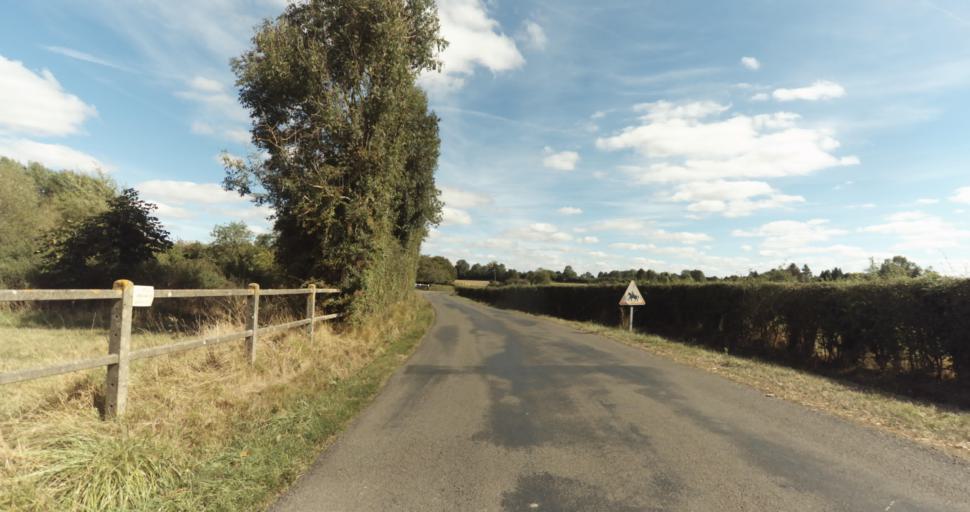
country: FR
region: Lower Normandy
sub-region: Departement de l'Orne
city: Vimoutiers
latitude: 48.9328
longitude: 0.2345
